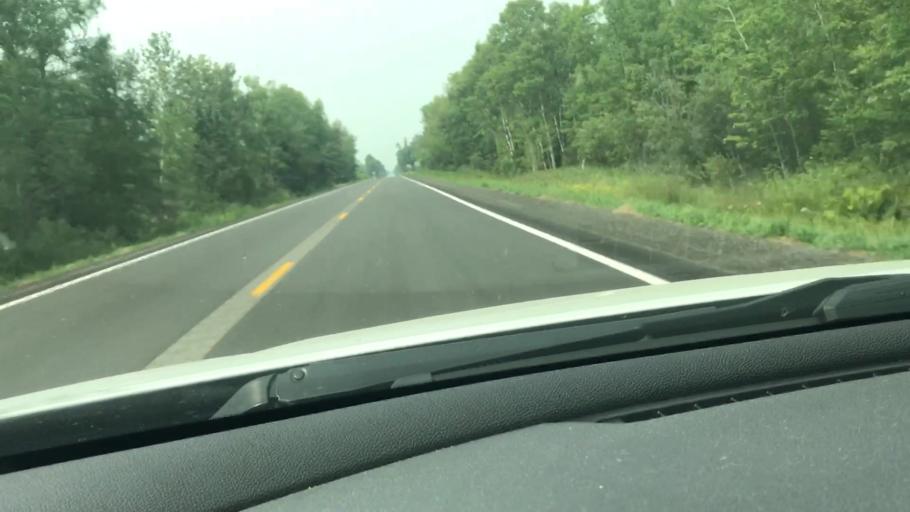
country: US
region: Minnesota
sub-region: Itasca County
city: Cohasset
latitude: 47.3652
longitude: -93.8745
